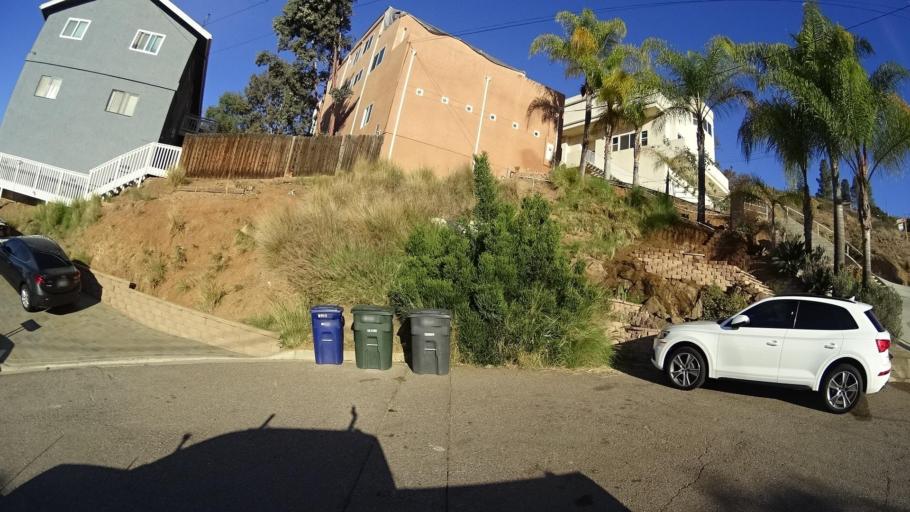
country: US
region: California
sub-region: San Diego County
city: La Presa
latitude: 32.7188
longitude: -116.9903
